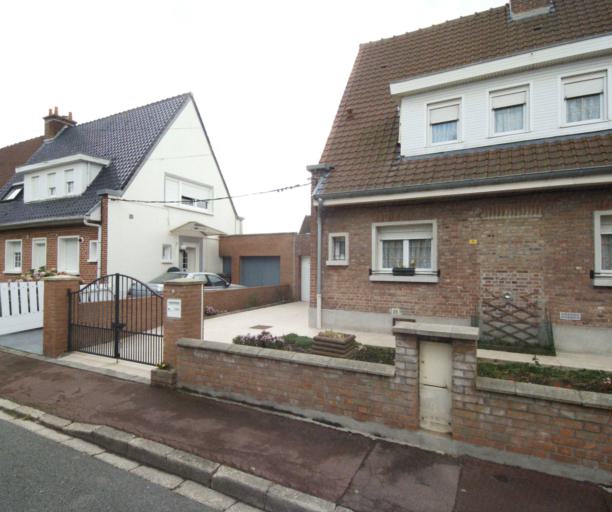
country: FR
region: Nord-Pas-de-Calais
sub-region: Departement du Nord
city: Lomme
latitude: 50.6439
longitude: 2.9841
